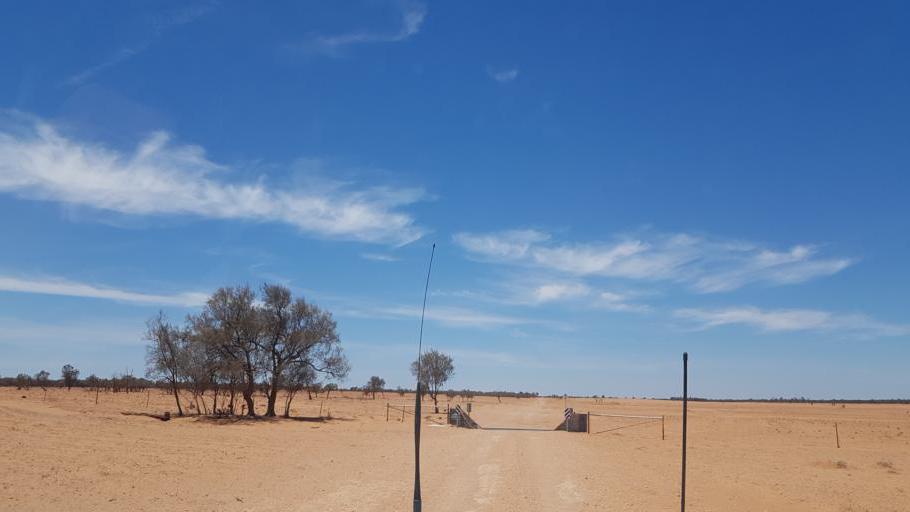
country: AU
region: New South Wales
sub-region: Wentworth
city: Dareton
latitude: -33.3488
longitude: 141.4636
